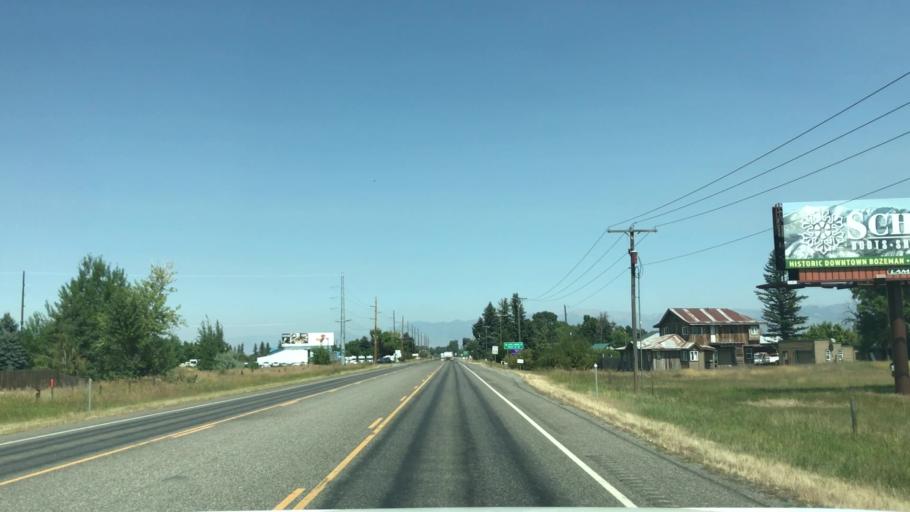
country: US
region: Montana
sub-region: Gallatin County
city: Four Corners
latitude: 45.6509
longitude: -111.1908
